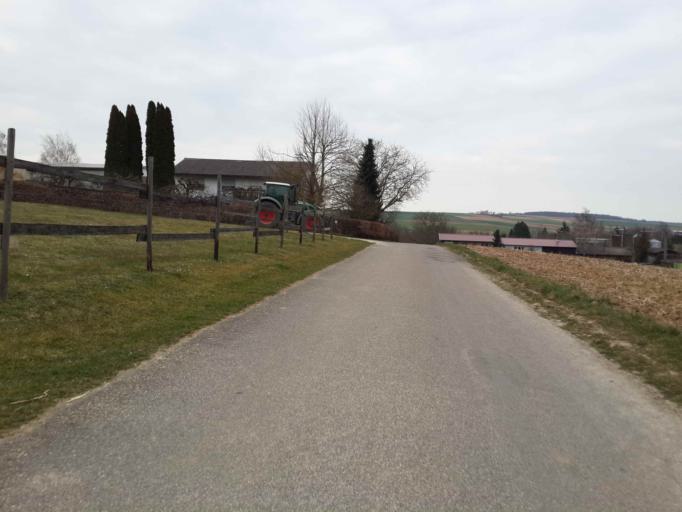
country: DE
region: Baden-Wuerttemberg
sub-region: Regierungsbezirk Stuttgart
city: Leingarten
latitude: 49.1391
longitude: 9.0922
